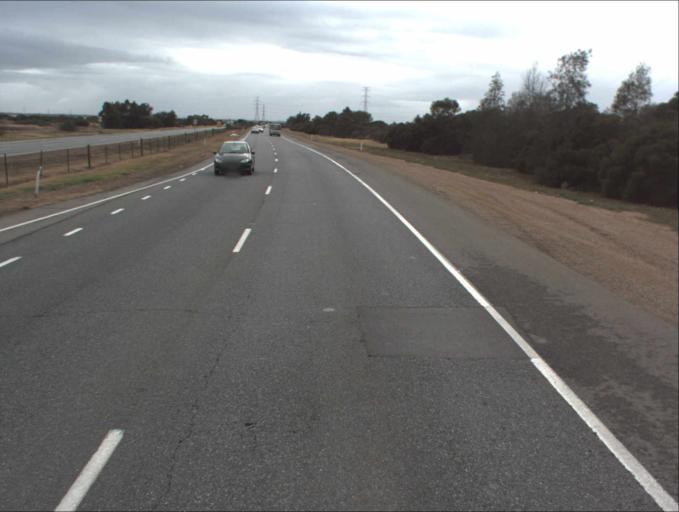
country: AU
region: South Australia
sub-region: Port Adelaide Enfield
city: Enfield
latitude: -34.8294
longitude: 138.5850
